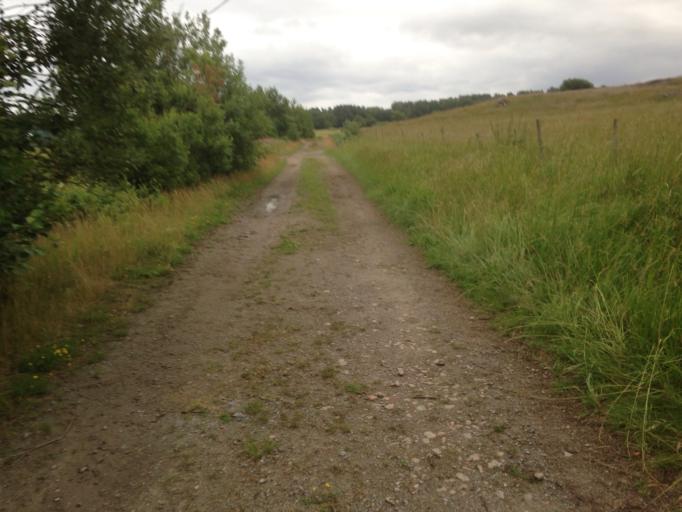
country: SE
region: Vaestra Goetaland
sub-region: Goteborg
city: Majorna
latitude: 57.8001
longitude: 11.8957
